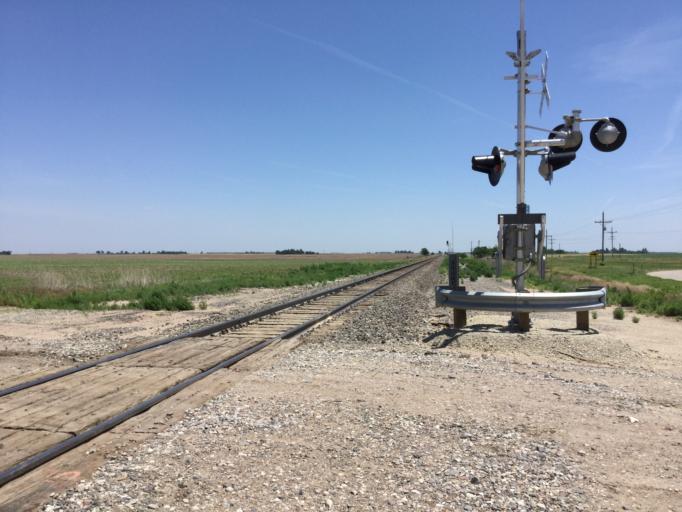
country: US
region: Kansas
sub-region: Edwards County
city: Kinsley
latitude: 37.9401
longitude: -99.2434
